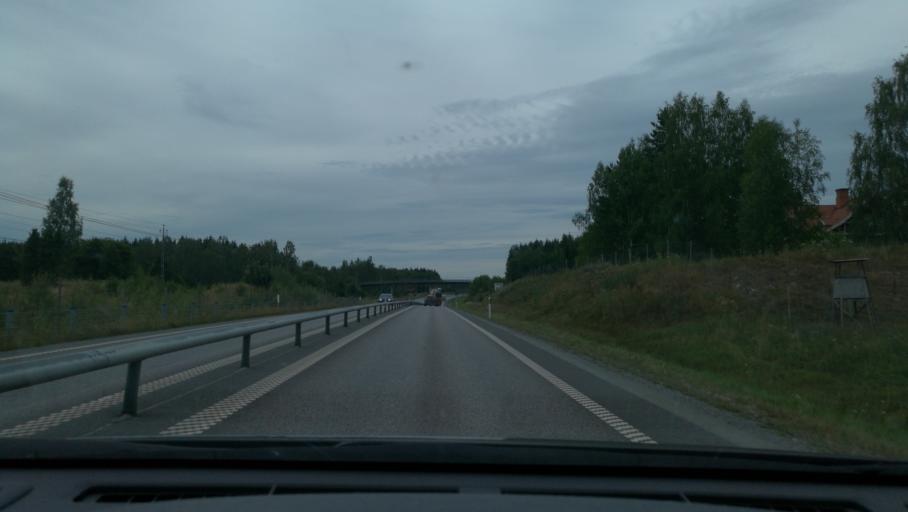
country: SE
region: Soedermanland
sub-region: Katrineholms Kommun
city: Katrineholm
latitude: 58.9215
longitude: 16.1965
